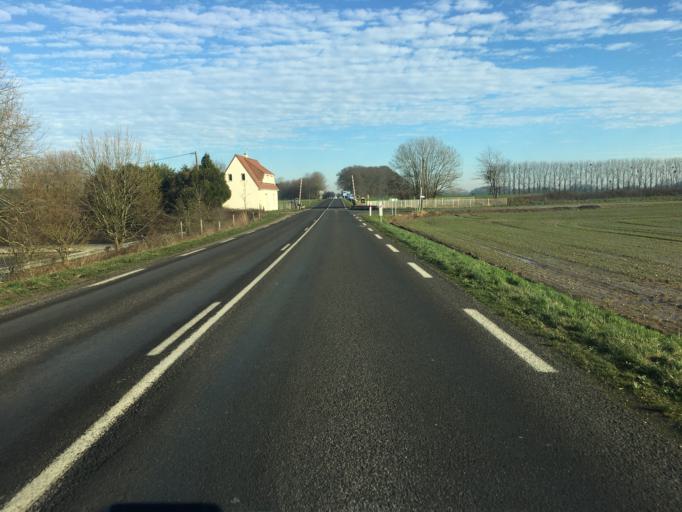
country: FR
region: Haute-Normandie
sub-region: Departement de la Seine-Maritime
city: Sainte-Marie-des-Champs
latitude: 49.6421
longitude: 0.8339
